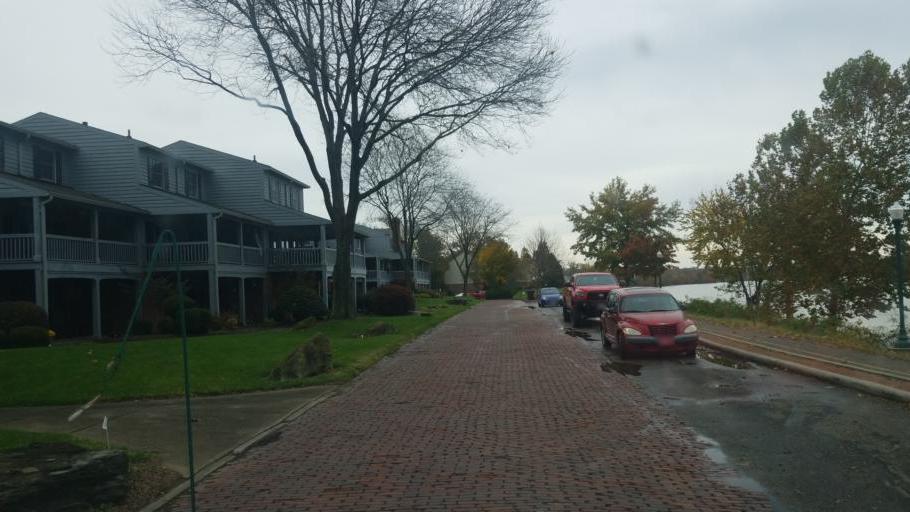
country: US
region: Ohio
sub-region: Washington County
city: Marietta
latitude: 39.4110
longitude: -81.4477
